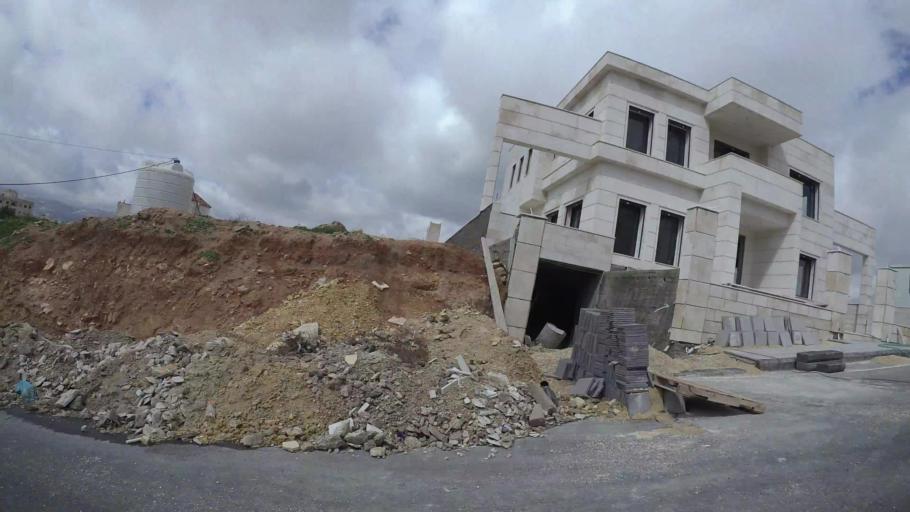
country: JO
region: Amman
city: Al Jubayhah
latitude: 32.0674
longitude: 35.8751
